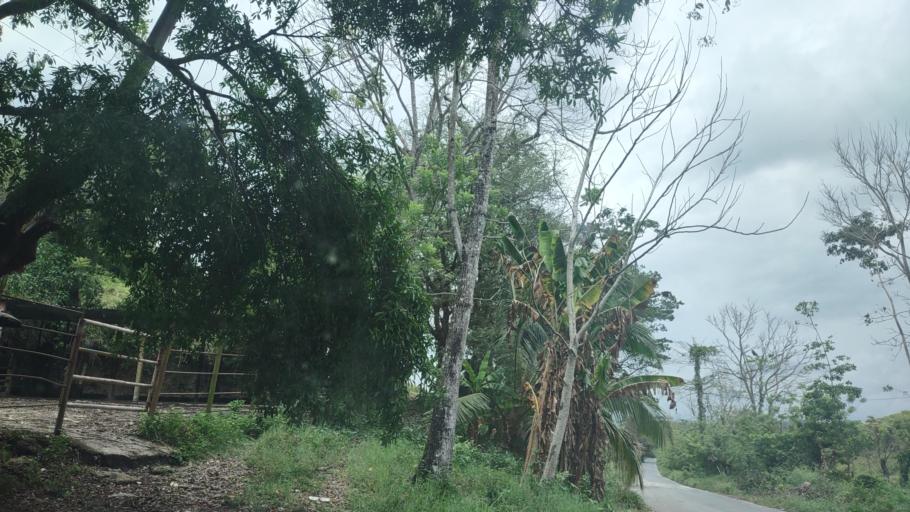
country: MX
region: Tabasco
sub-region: Huimanguillo
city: Francisco Rueda
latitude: 17.5239
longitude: -94.1348
